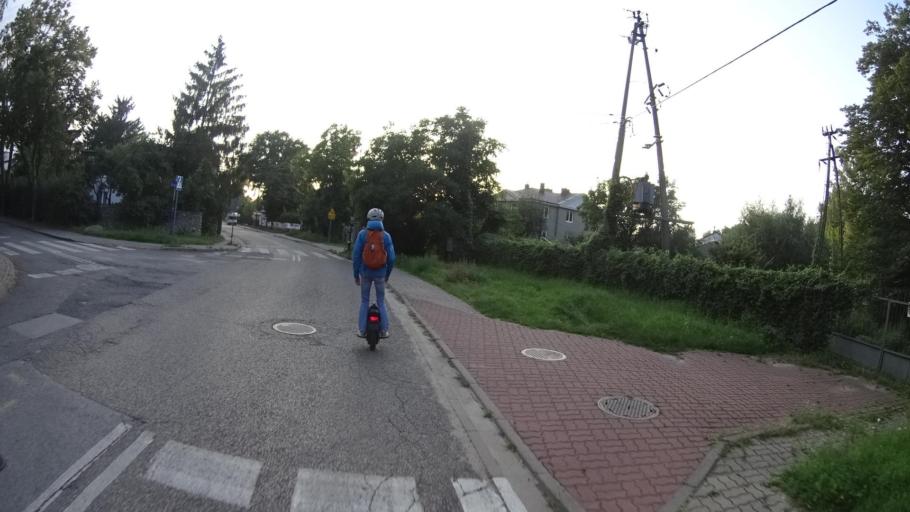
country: PL
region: Masovian Voivodeship
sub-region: Warszawa
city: Bielany
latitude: 52.3074
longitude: 20.9356
